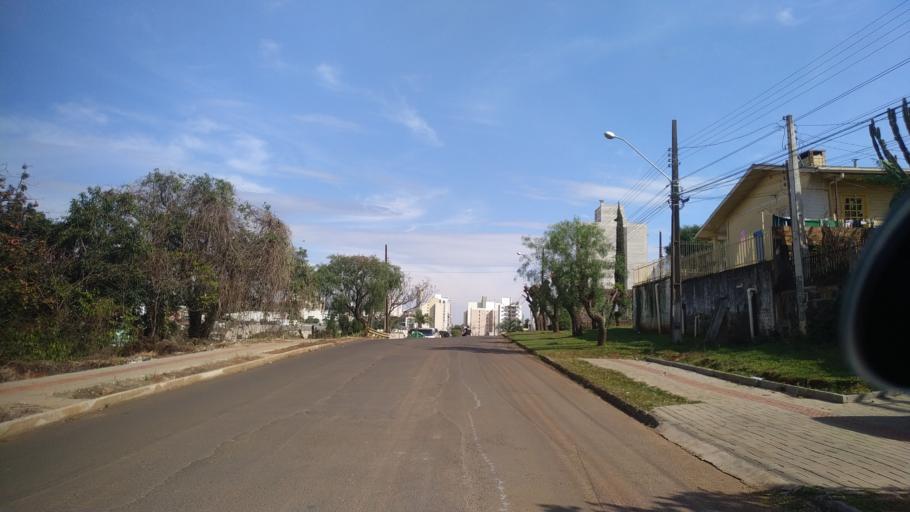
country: BR
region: Santa Catarina
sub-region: Chapeco
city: Chapeco
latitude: -27.1066
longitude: -52.6022
